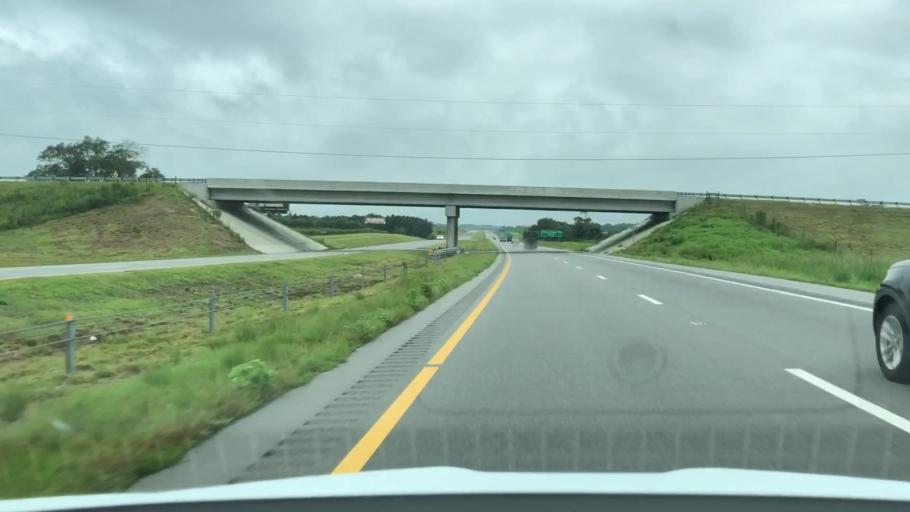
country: US
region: North Carolina
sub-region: Wayne County
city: Elroy
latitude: 35.4032
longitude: -77.8774
